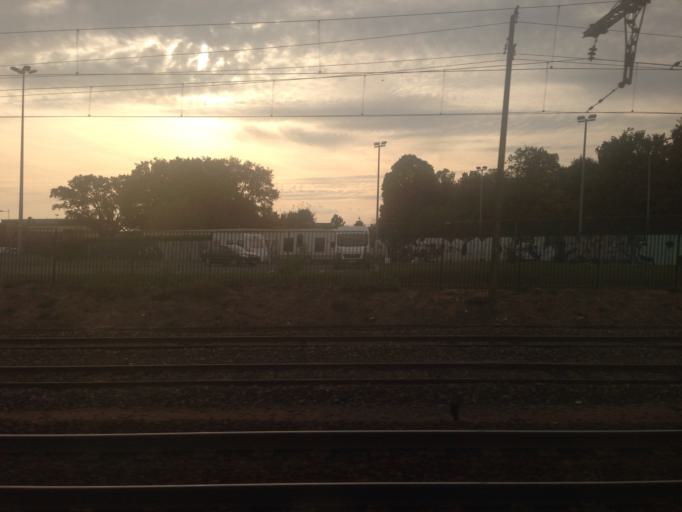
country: FR
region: Centre
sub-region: Departement du Loiret
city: Saran
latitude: 47.9479
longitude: 1.8964
